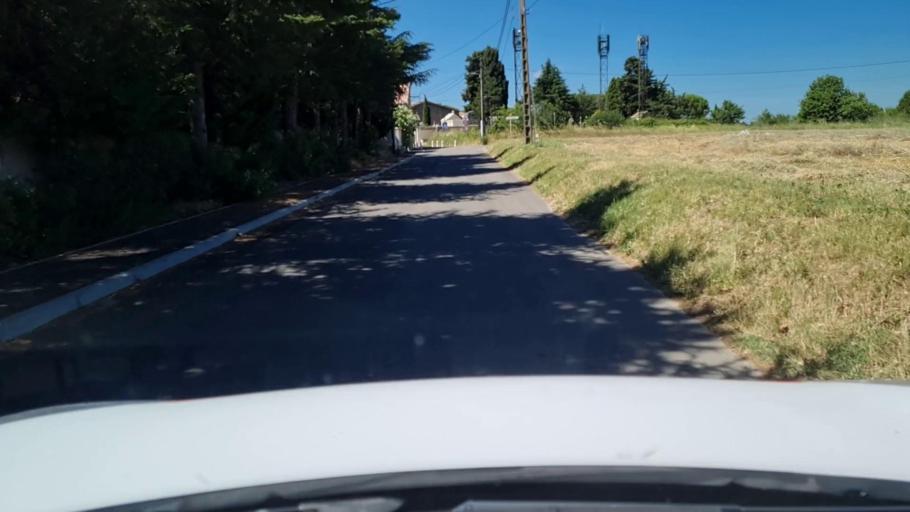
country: FR
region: Languedoc-Roussillon
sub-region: Departement du Gard
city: Saint-Mamert-du-Gard
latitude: 43.8552
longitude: 4.1597
